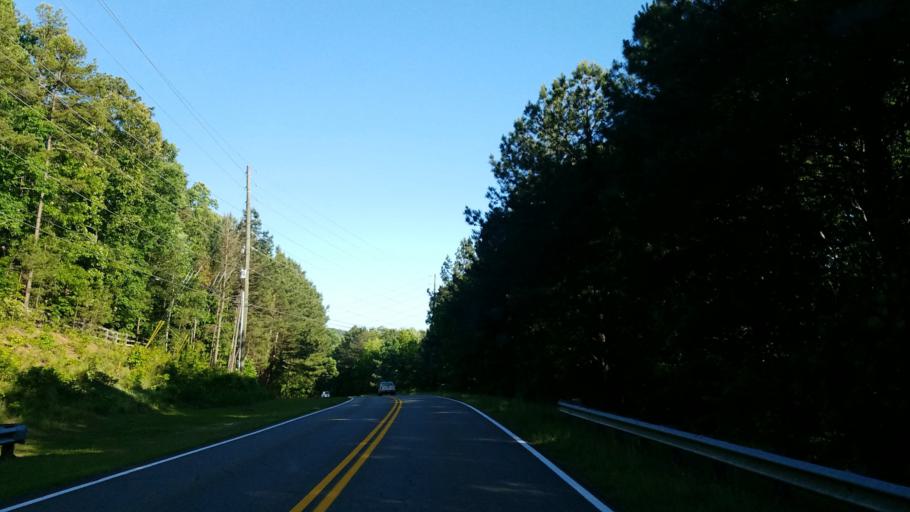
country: US
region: Georgia
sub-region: Cherokee County
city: Holly Springs
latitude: 34.1773
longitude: -84.5355
